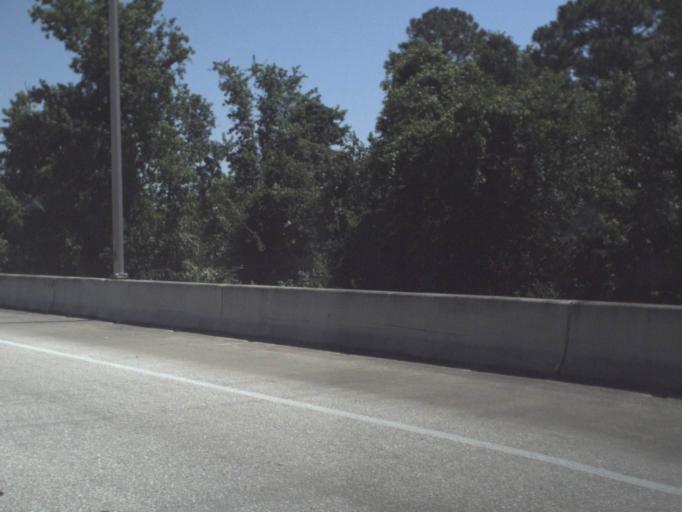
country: US
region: Florida
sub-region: Duval County
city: Neptune Beach
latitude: 30.2805
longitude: -81.5215
